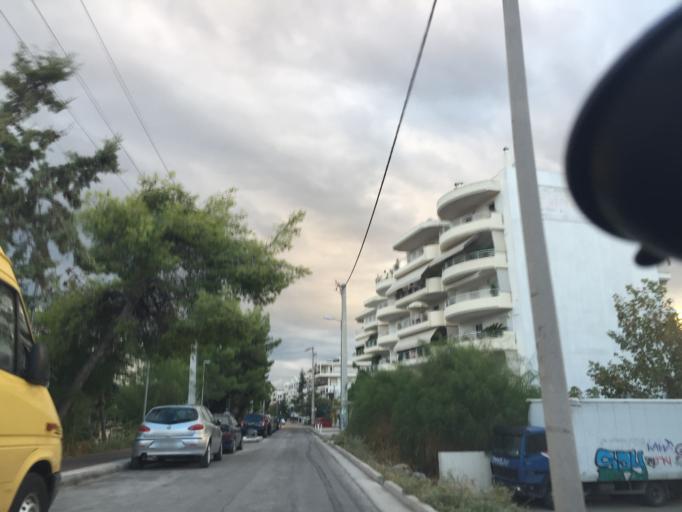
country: GR
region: Attica
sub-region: Nomarchia Athinas
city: Moskhaton
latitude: 37.9502
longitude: 23.6861
